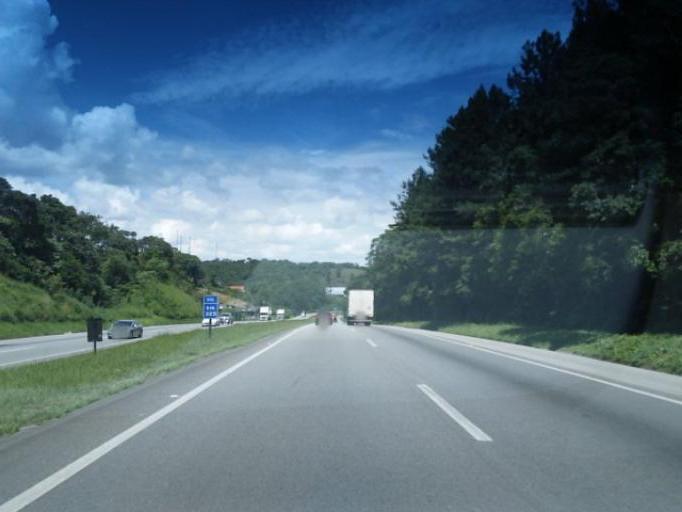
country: BR
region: Sao Paulo
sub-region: Juquitiba
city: Juquitiba
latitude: -23.9405
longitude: -47.0544
